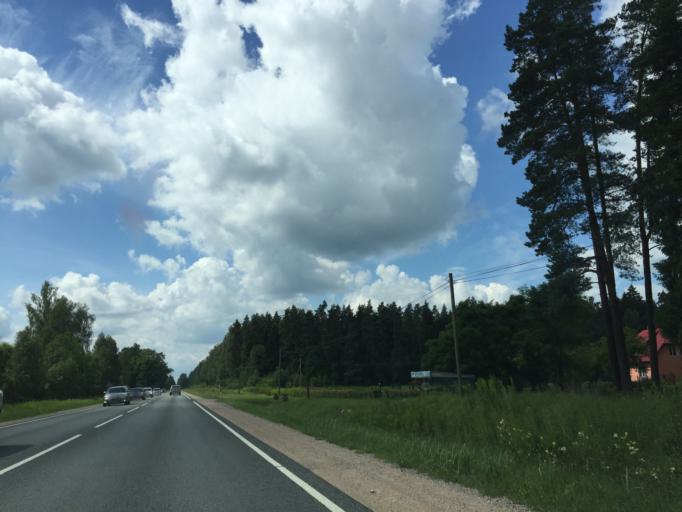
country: LV
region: Ozolnieku
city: Ozolnieki
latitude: 56.7148
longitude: 23.8344
